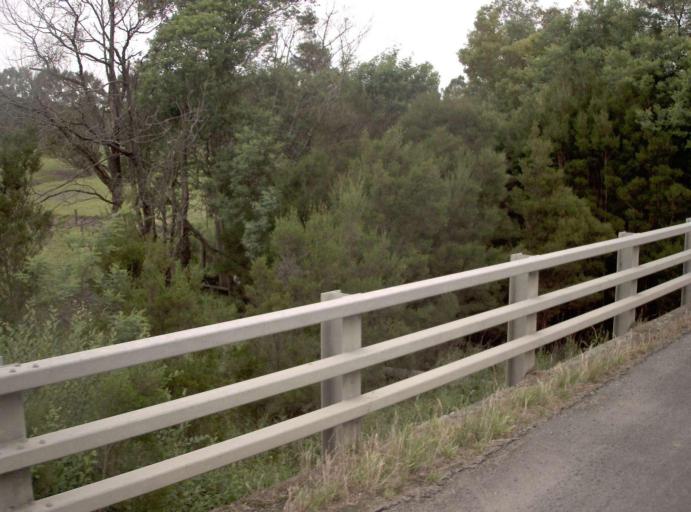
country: AU
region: Victoria
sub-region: Bass Coast
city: North Wonthaggi
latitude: -38.5242
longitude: 145.9519
